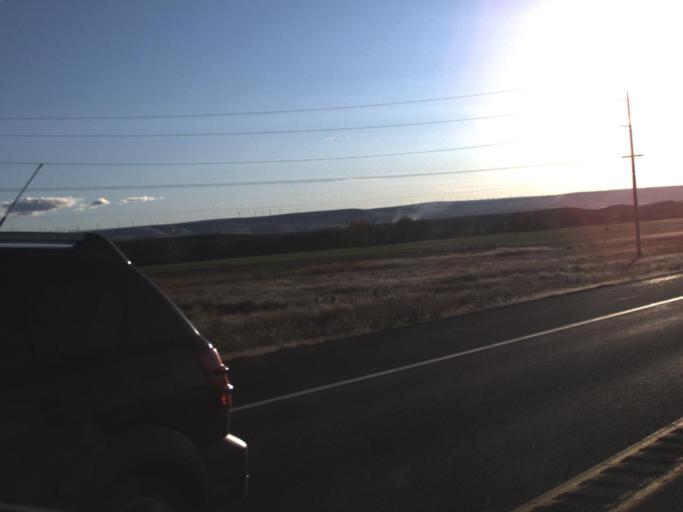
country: US
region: Washington
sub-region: Walla Walla County
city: Garrett
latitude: 46.0503
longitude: -118.5174
